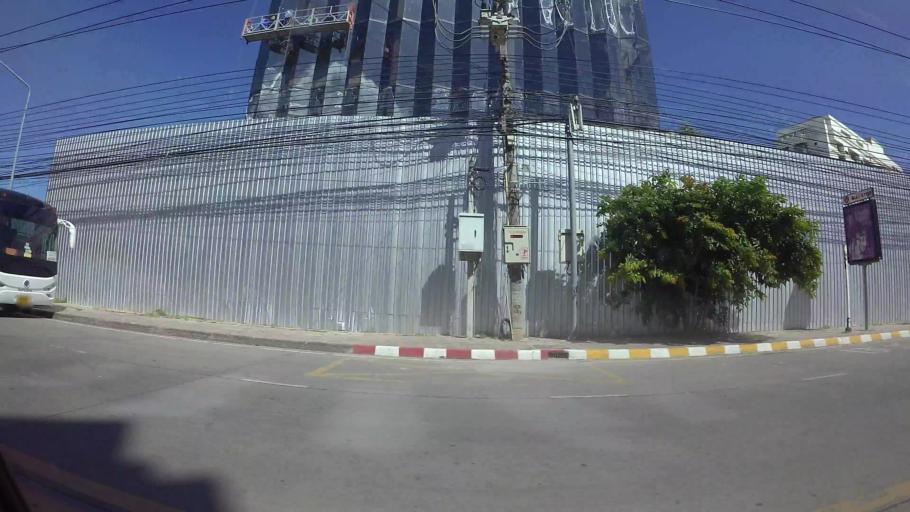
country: TH
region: Chon Buri
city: Phatthaya
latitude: 12.9477
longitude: 100.8966
